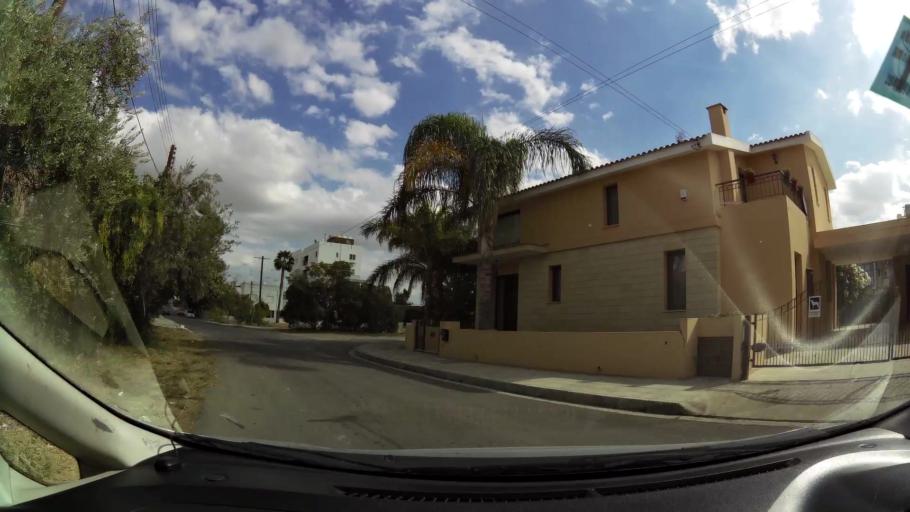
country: CY
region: Lefkosia
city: Nicosia
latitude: 35.1885
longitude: 33.3904
